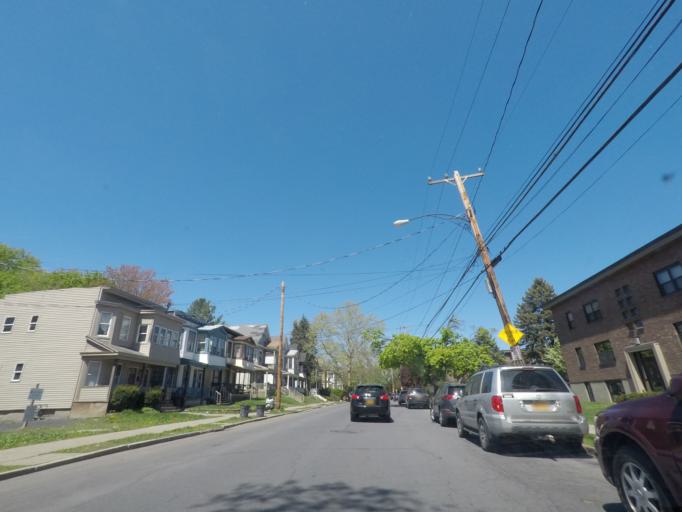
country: US
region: New York
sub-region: Albany County
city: Albany
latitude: 42.6672
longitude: -73.7646
